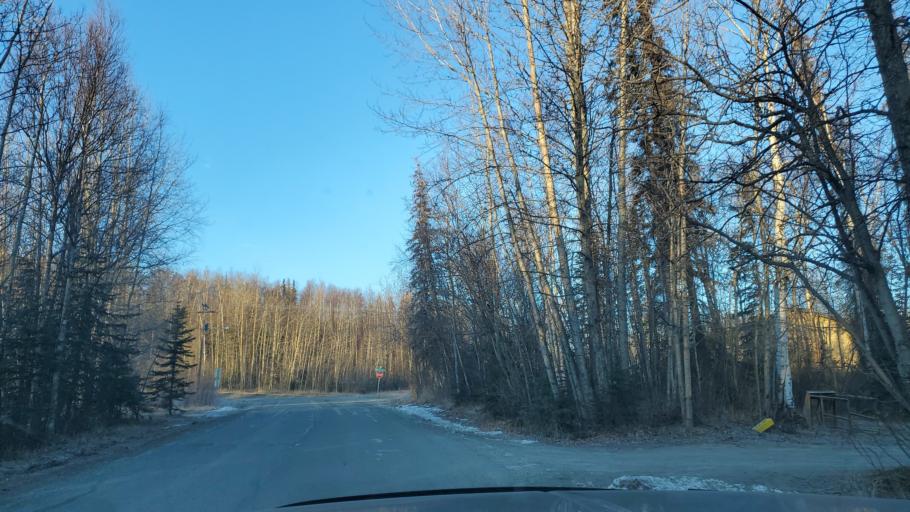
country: US
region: Alaska
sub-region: Matanuska-Susitna Borough
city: Tanaina
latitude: 61.6092
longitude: -149.4041
